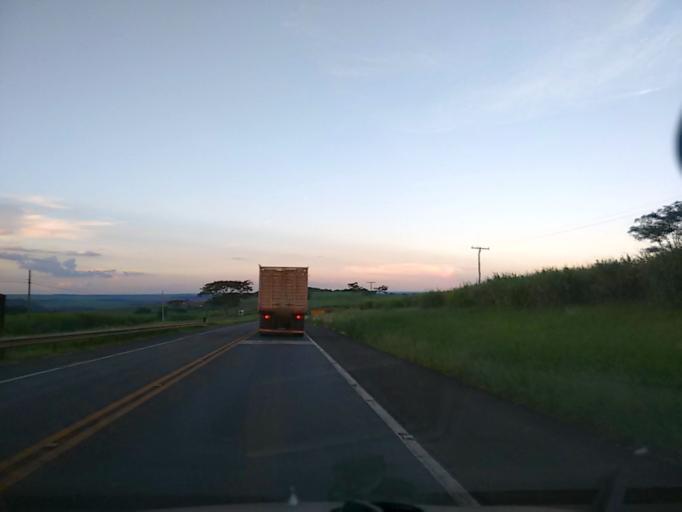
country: BR
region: Sao Paulo
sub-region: Boa Esperanca Do Sul
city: Boa Esperanca do Sul
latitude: -22.1233
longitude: -48.4574
